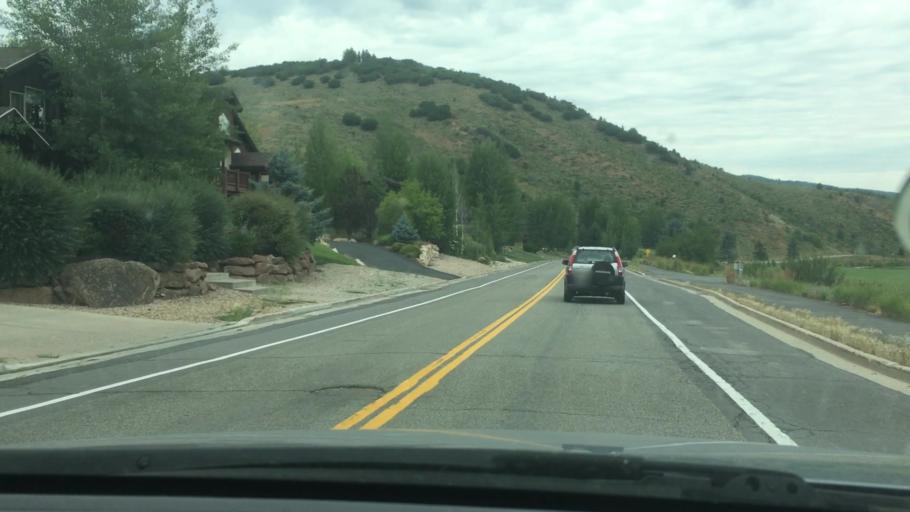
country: US
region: Utah
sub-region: Summit County
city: Summit Park
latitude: 40.7638
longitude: -111.5806
